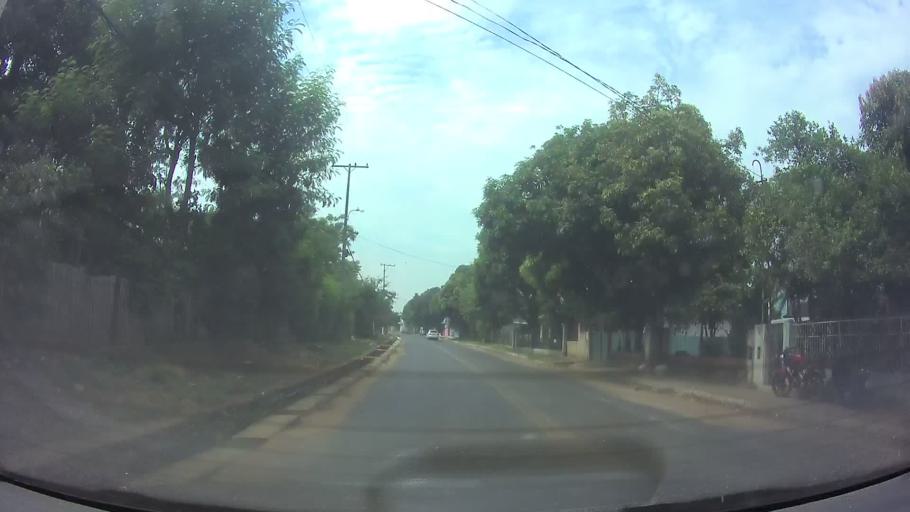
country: PY
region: Central
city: Fernando de la Mora
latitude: -25.2943
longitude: -57.5117
